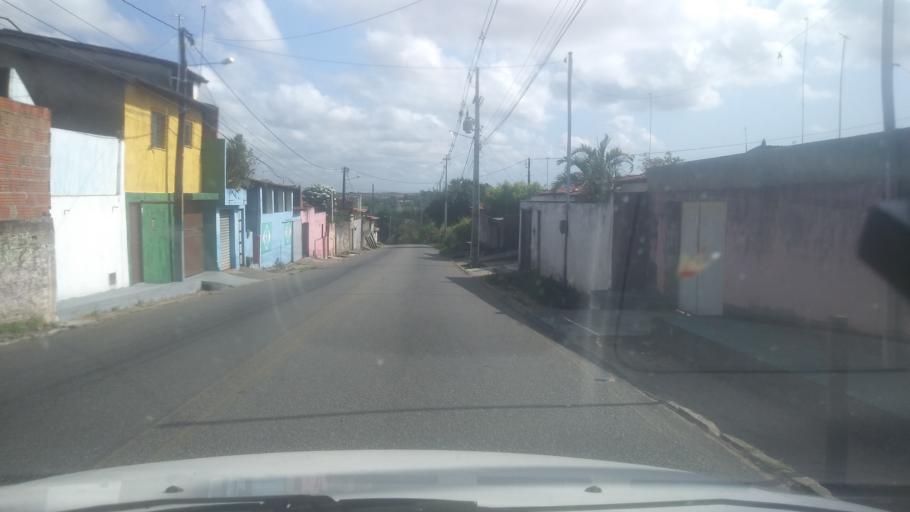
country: BR
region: Rio Grande do Norte
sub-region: Extremoz
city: Extremoz
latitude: -5.7119
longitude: -35.2777
